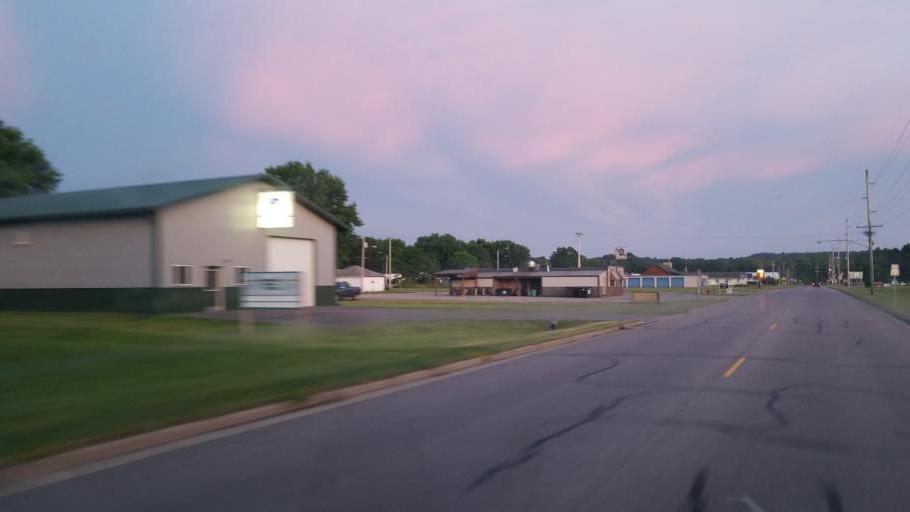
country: US
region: Wisconsin
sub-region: Juneau County
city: Elroy
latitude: 43.6846
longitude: -90.2661
